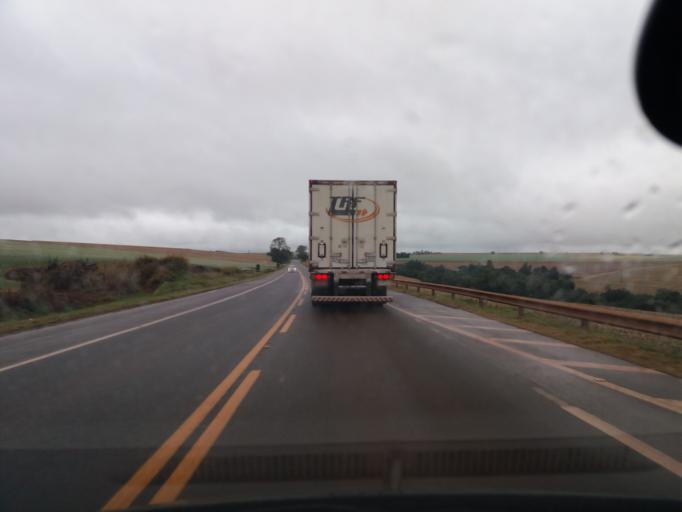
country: BR
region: Parana
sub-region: Campo Mourao
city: Campo Mourao
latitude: -24.3308
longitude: -52.6570
